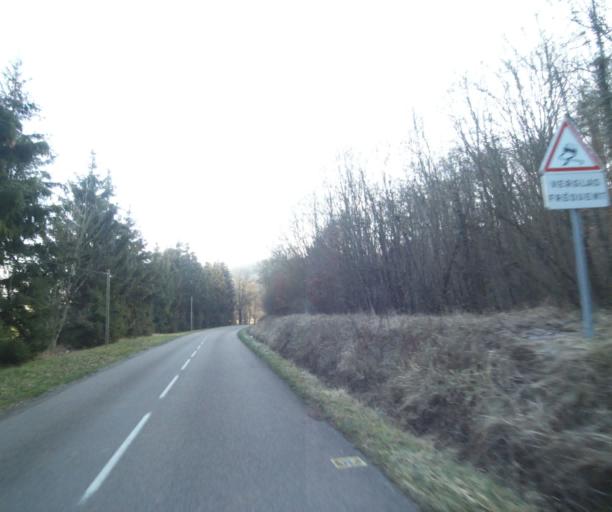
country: FR
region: Champagne-Ardenne
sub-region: Departement de la Haute-Marne
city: Bienville
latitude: 48.5572
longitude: 5.0863
